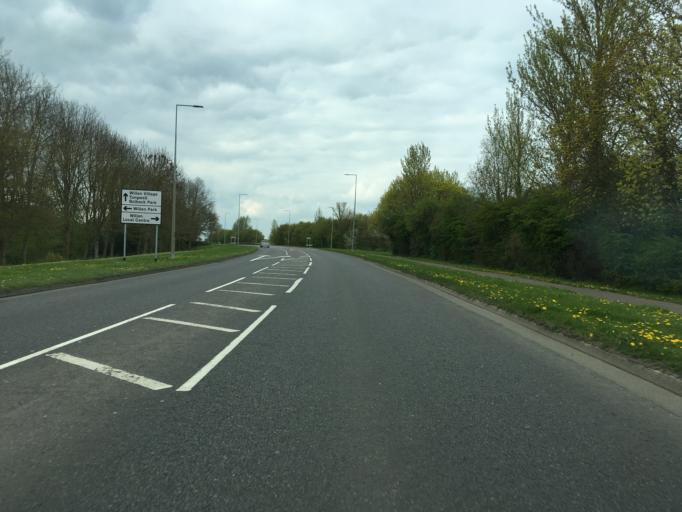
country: GB
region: England
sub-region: Milton Keynes
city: Newport Pagnell
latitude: 52.0589
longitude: -0.7293
